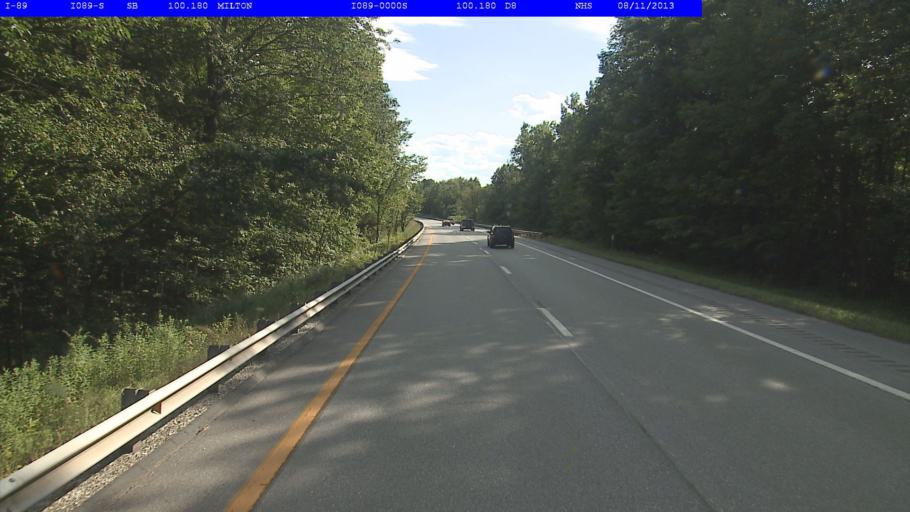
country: US
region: Vermont
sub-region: Chittenden County
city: Milton
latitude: 44.6212
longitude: -73.1600
